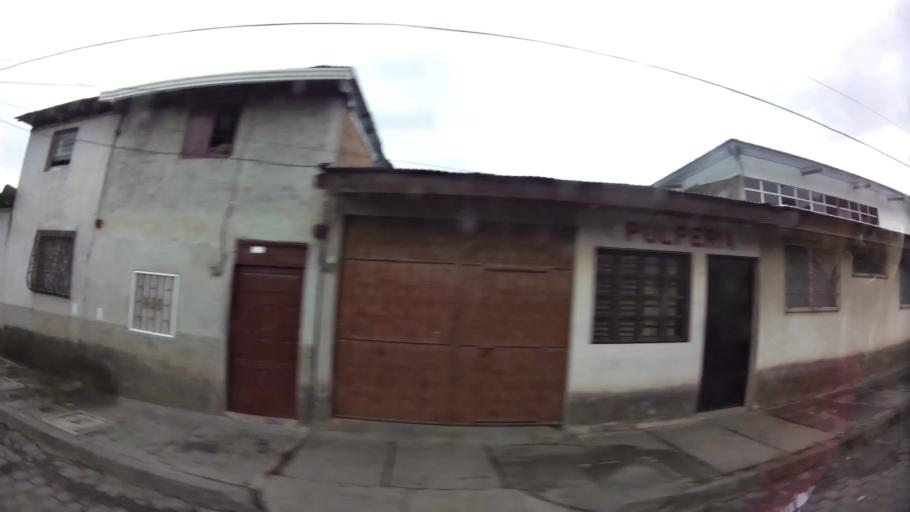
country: NI
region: Jinotega
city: Jinotega
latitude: 13.0878
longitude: -85.9985
